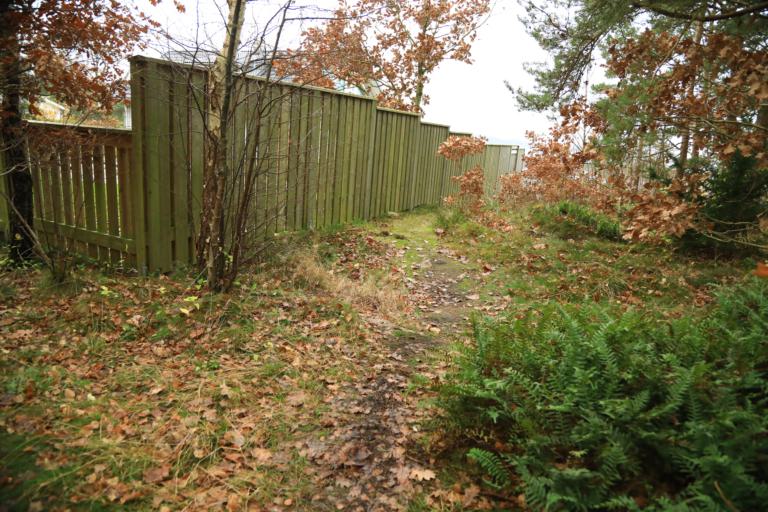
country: SE
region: Halland
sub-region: Varbergs Kommun
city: Varberg
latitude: 57.1709
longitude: 12.2105
